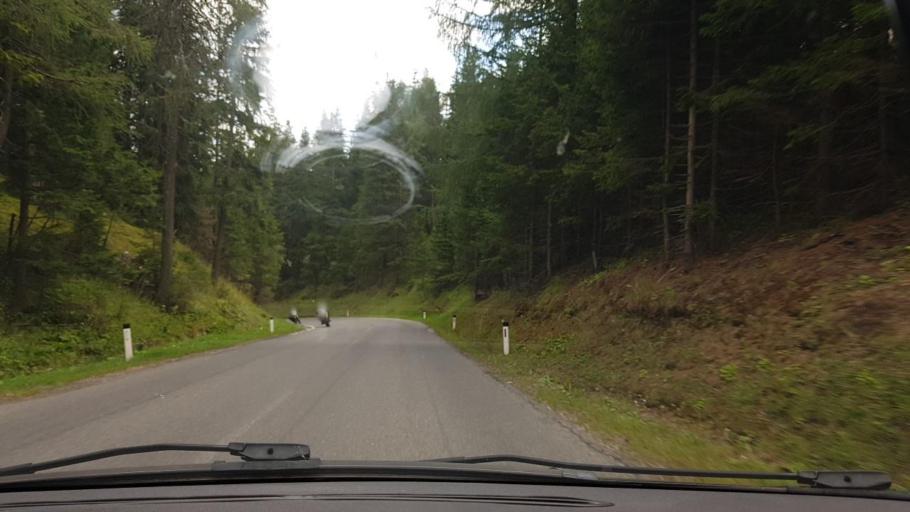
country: AT
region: Salzburg
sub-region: Politischer Bezirk Tamsweg
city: Sankt Michael im Lungau
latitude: 47.0550
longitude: 13.6164
